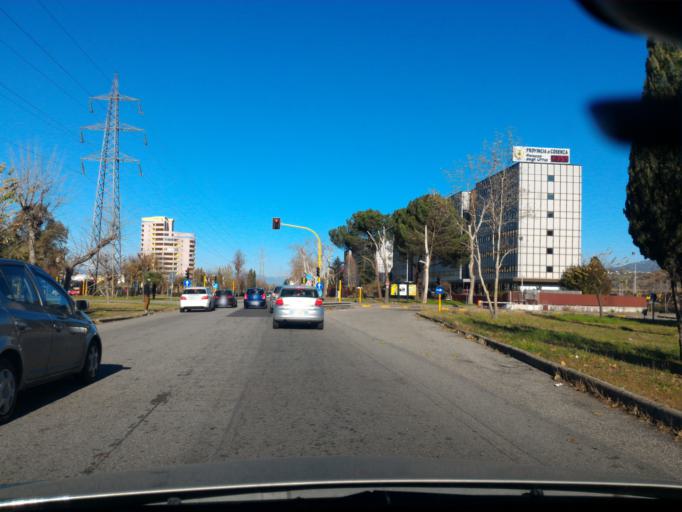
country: IT
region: Calabria
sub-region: Provincia di Cosenza
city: Cosenza
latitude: 39.3186
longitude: 16.2576
